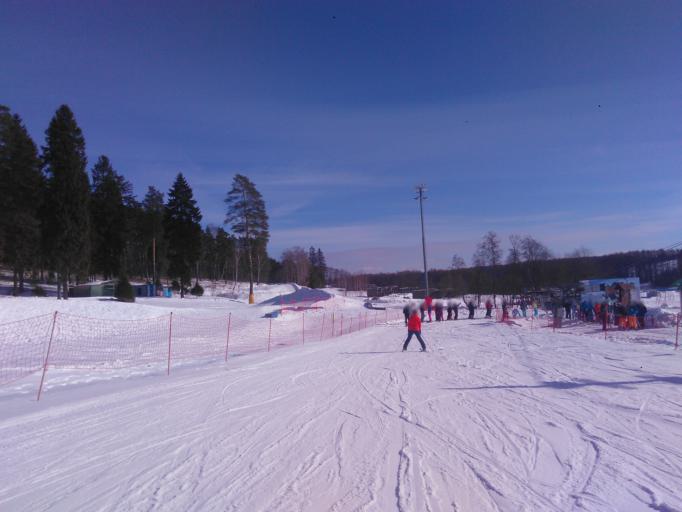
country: RU
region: Moskovskaya
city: Dedenevo
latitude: 56.2745
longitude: 37.5708
